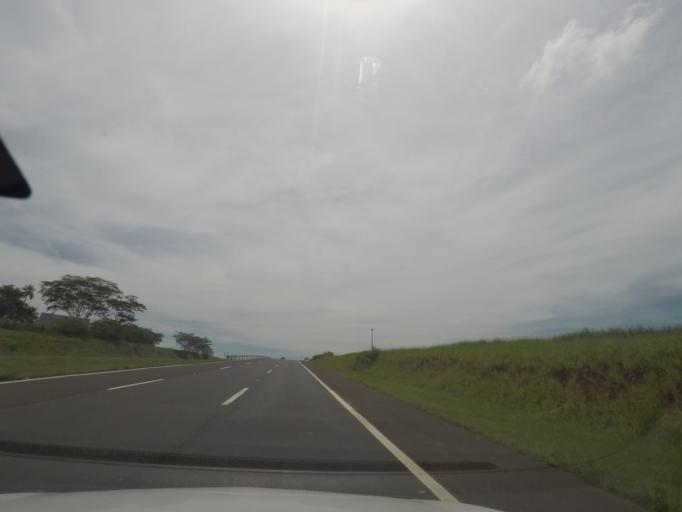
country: BR
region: Sao Paulo
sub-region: Bebedouro
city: Bebedouro
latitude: -20.9681
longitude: -48.4409
